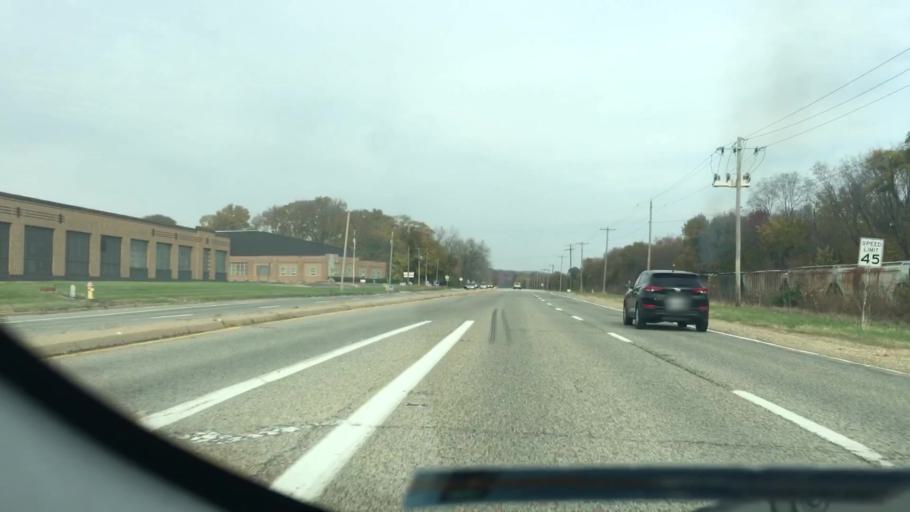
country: US
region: Illinois
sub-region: Peoria County
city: Peoria Heights
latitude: 40.7589
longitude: -89.5652
